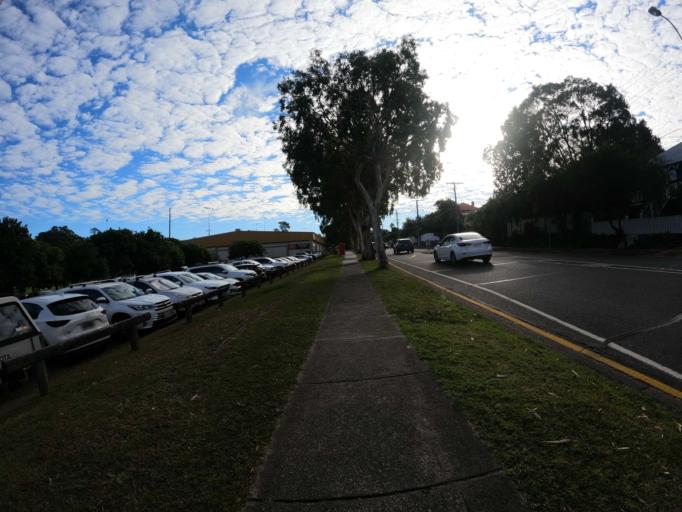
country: AU
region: Queensland
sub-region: Brisbane
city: Windsor
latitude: -27.4406
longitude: 153.0257
